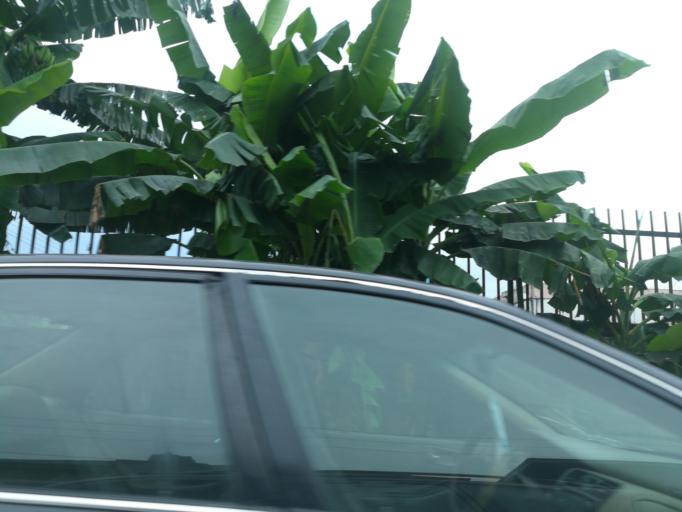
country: NG
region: Rivers
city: Port Harcourt
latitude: 4.7630
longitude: 7.0207
